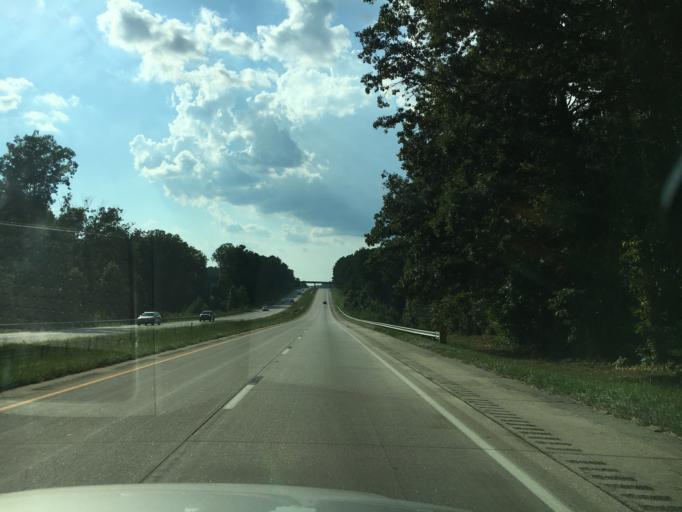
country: US
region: South Carolina
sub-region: Laurens County
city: Watts Mills
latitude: 34.5286
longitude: -81.9253
